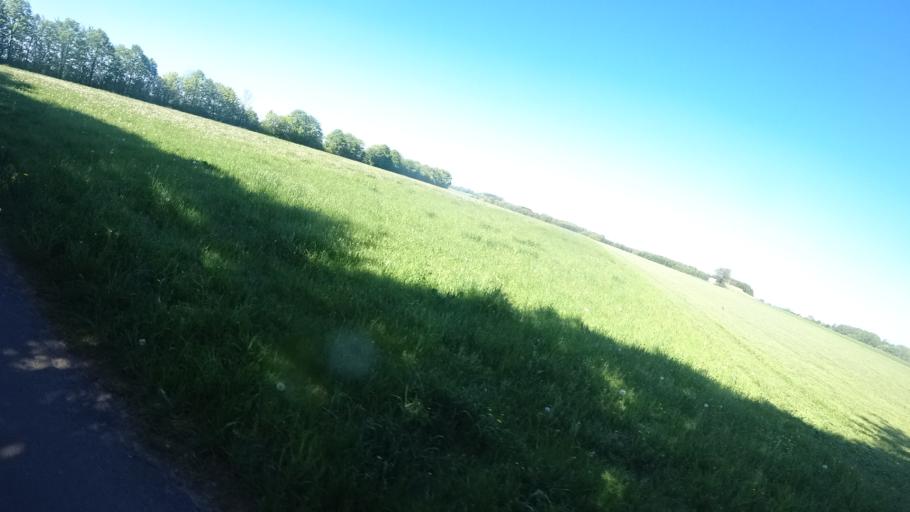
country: DE
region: Rheinland-Pfalz
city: Neunkhausen
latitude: 50.7204
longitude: 7.9030
